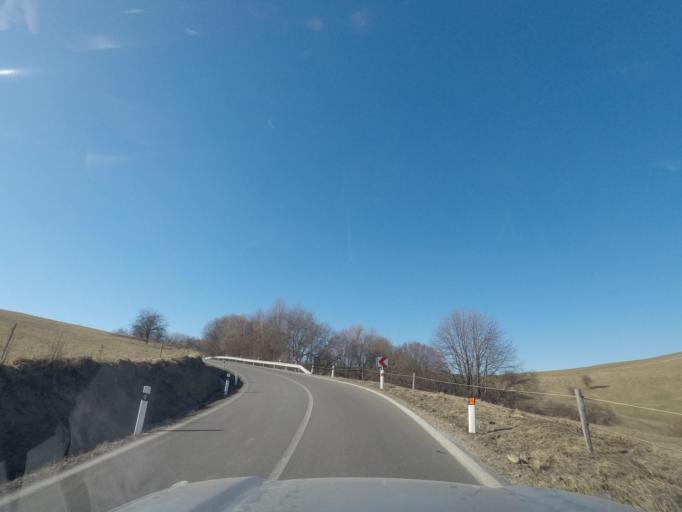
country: SK
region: Presovsky
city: Snina
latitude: 49.0998
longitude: 22.1479
